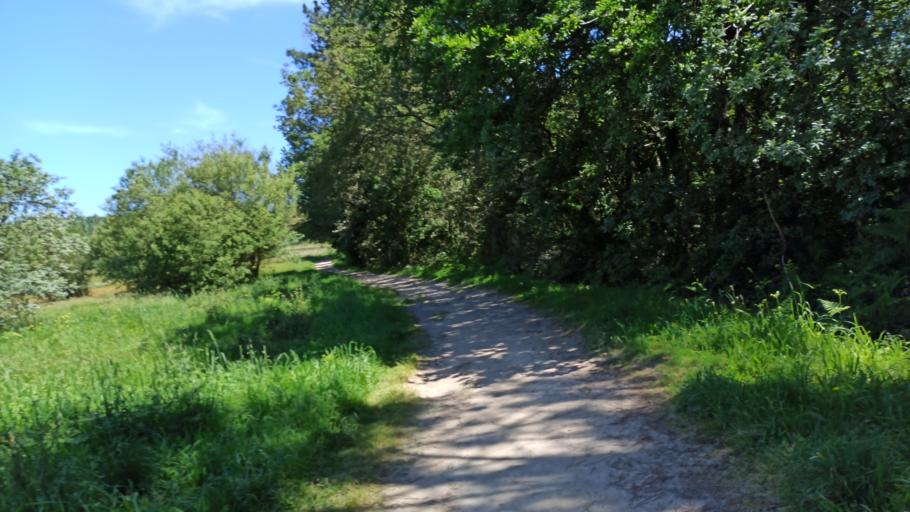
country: ES
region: Galicia
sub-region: Provincia da Coruna
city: Negreira
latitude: 42.9129
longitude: -8.7320
